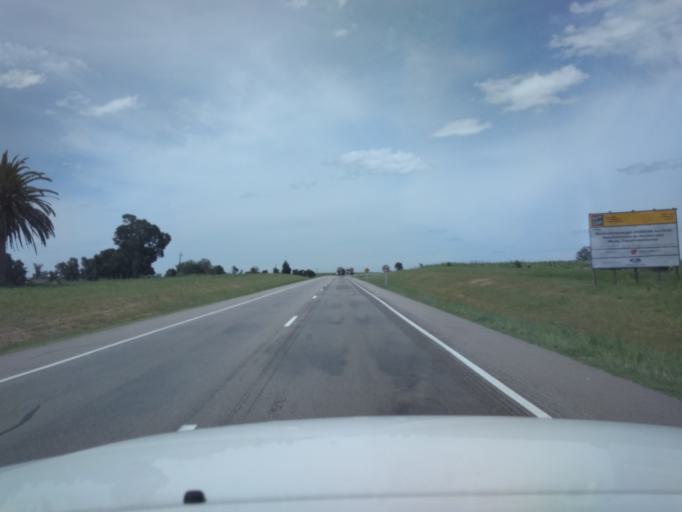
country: UY
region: Florida
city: Cardal
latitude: -34.3208
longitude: -56.2428
